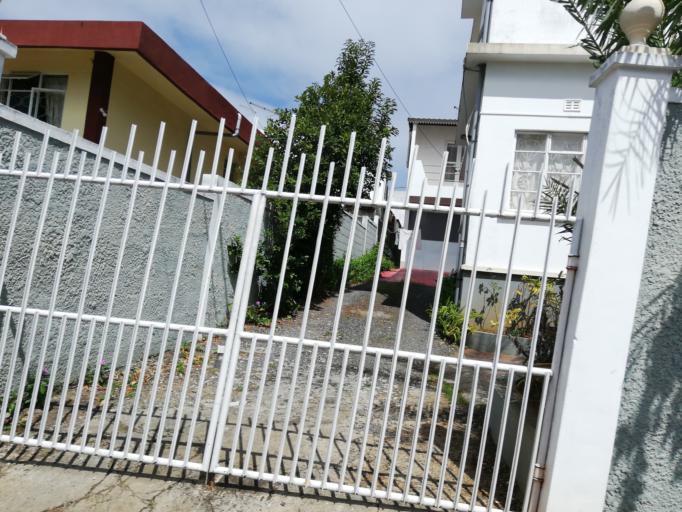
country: MU
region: Moka
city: Moka
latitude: -20.2155
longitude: 57.4710
